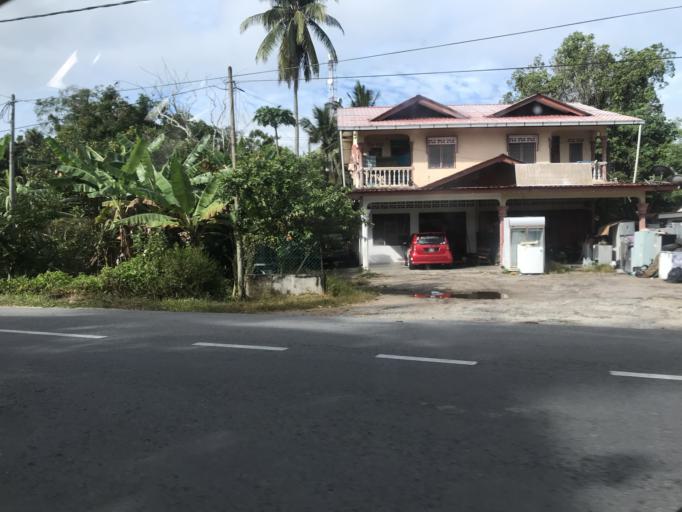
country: MY
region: Kelantan
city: Kota Bharu
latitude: 6.1217
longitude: 102.1867
